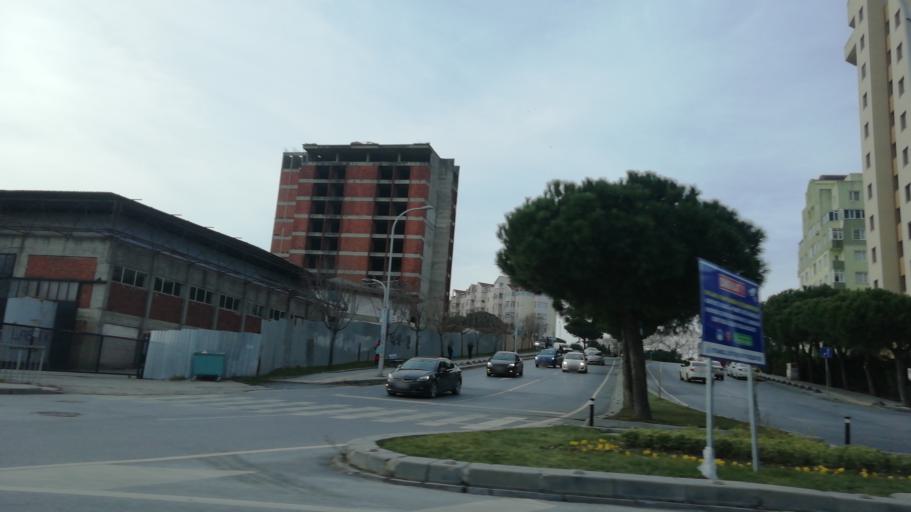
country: TR
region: Istanbul
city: Basaksehir
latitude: 41.1076
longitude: 28.7948
